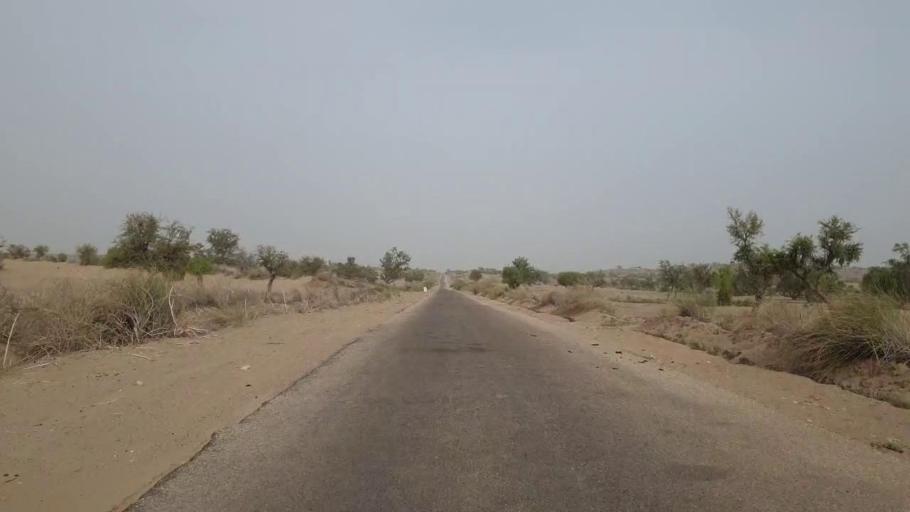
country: PK
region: Sindh
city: Islamkot
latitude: 24.5648
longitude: 70.3329
